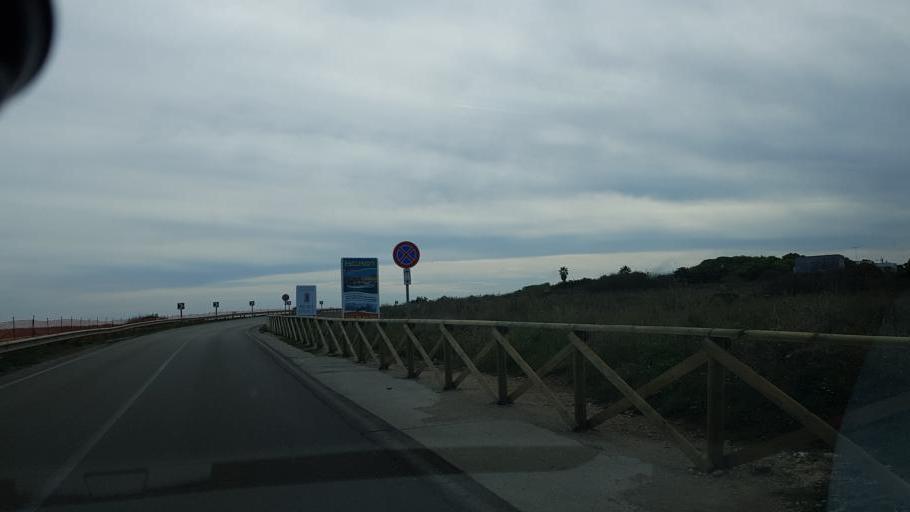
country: IT
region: Apulia
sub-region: Provincia di Lecce
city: Borgagne
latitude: 40.2839
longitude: 18.4297
